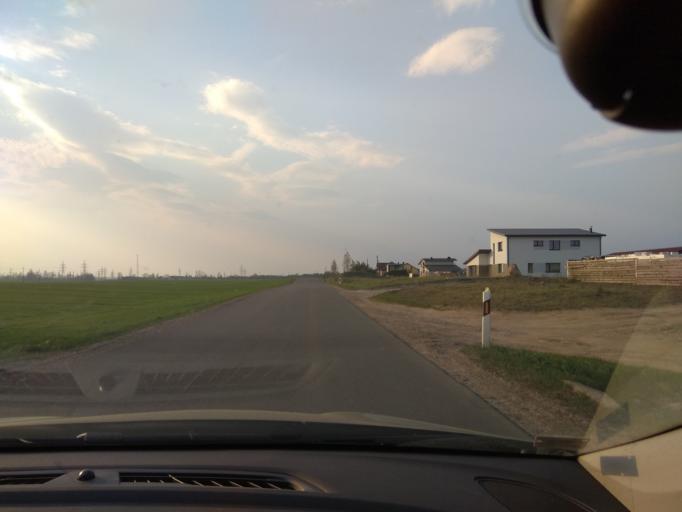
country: LT
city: Baltoji Voke
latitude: 54.6051
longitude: 25.1329
